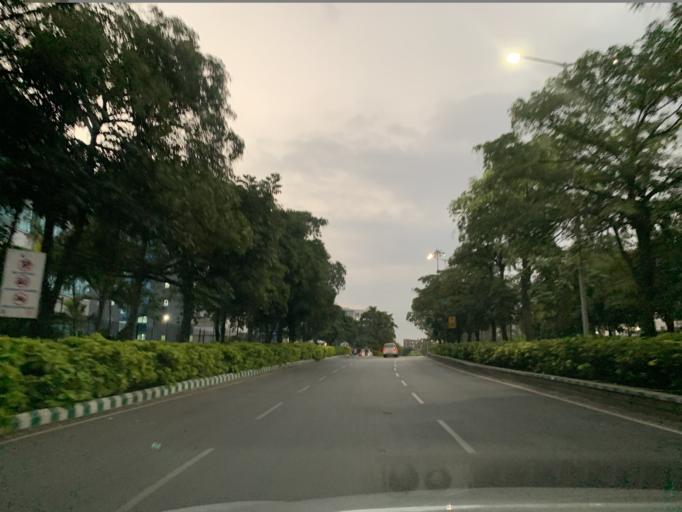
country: IN
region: Telangana
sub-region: Rangareddi
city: Kukatpalli
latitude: 17.4399
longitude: 78.3798
